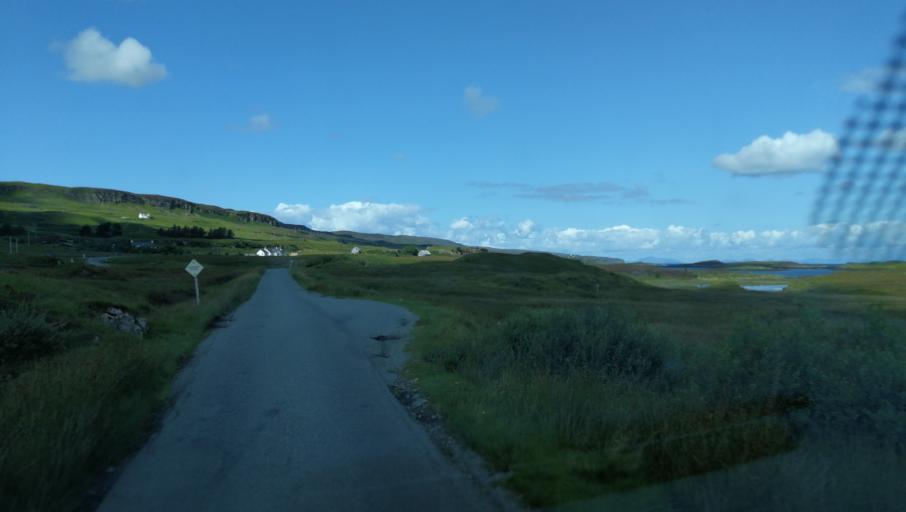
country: GB
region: Scotland
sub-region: Highland
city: Isle of Skye
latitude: 57.4303
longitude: -6.6187
